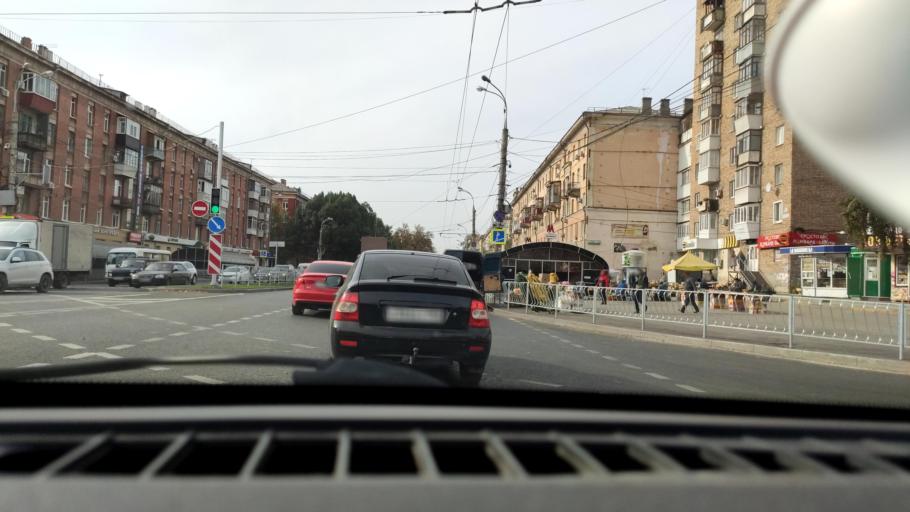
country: RU
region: Samara
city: Samara
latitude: 53.2129
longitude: 50.2484
